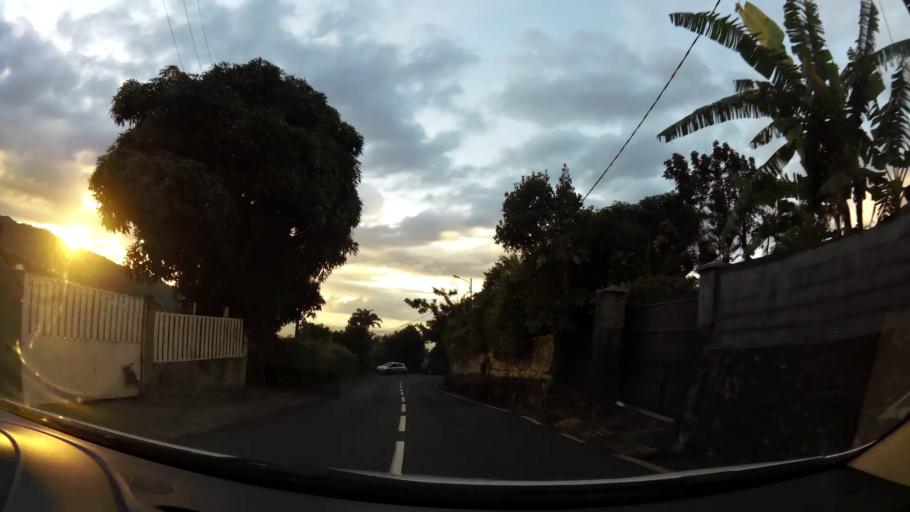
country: RE
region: Reunion
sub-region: Reunion
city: Saint-Denis
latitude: -20.9072
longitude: 55.4628
